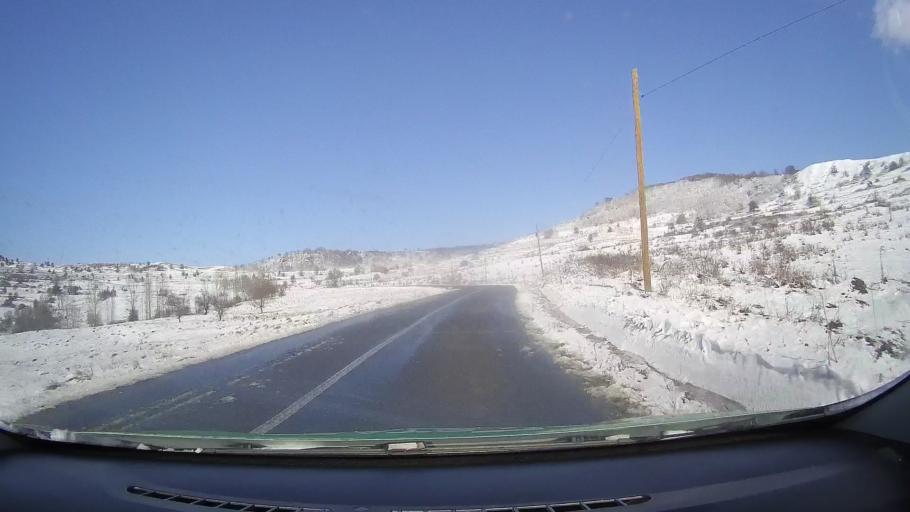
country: RO
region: Sibiu
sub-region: Comuna Avrig
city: Avrig
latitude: 45.7709
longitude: 24.3844
